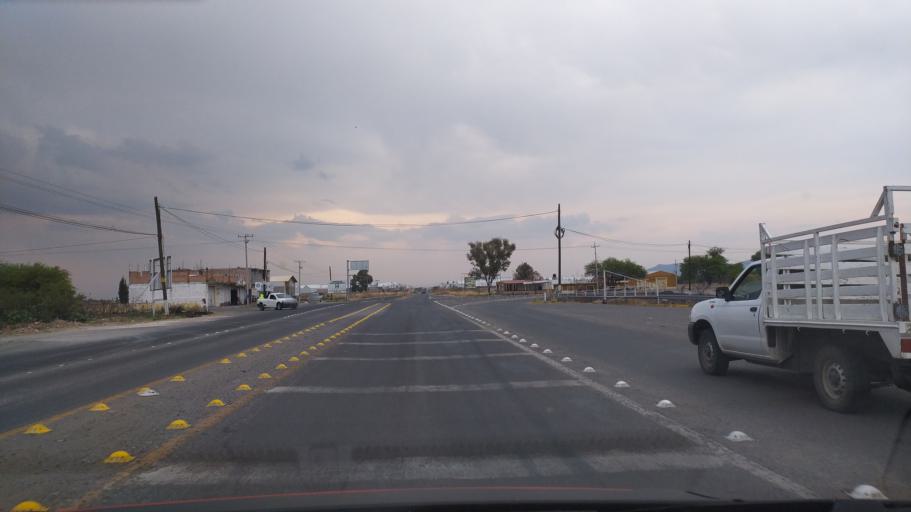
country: MX
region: Guanajuato
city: Ciudad Manuel Doblado
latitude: 20.7404
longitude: -101.9318
